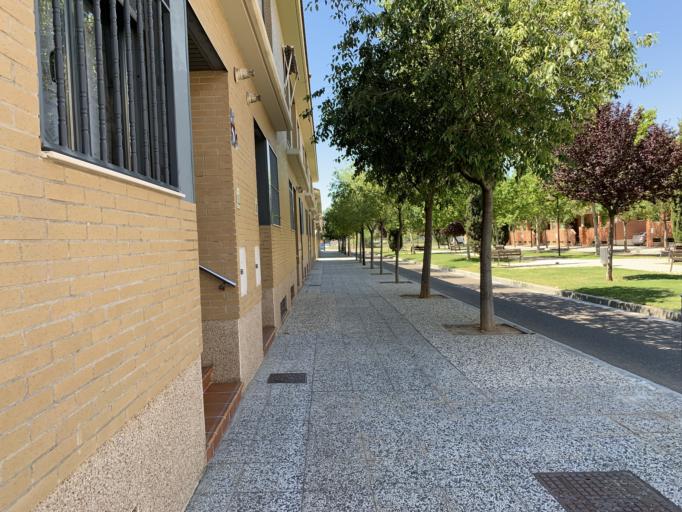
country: ES
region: Aragon
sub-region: Provincia de Zaragoza
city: Zaragoza
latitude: 41.6717
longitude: -0.8317
